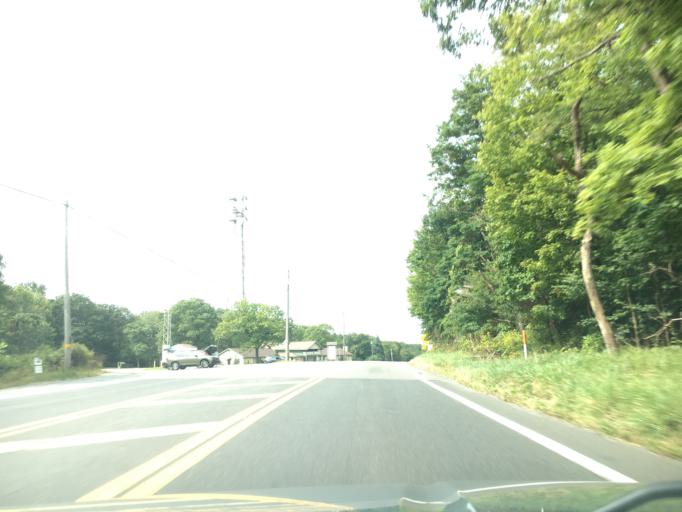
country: US
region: Pennsylvania
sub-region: Carbon County
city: Summit Hill
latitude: 40.7075
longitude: -75.8078
